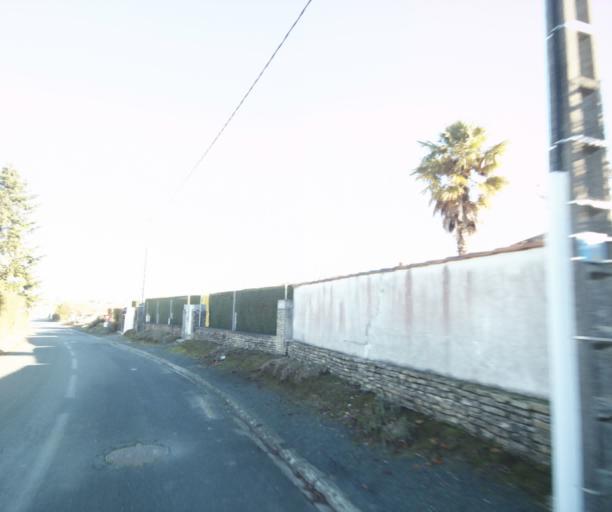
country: FR
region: Poitou-Charentes
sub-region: Departement de la Charente-Maritime
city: Fontcouverte
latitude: 45.7430
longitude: -0.5776
